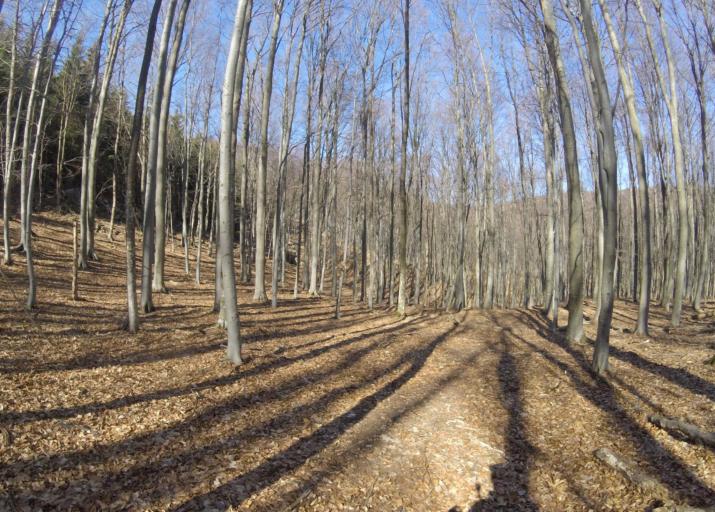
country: HU
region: Heves
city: Szilvasvarad
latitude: 48.0537
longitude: 20.4295
